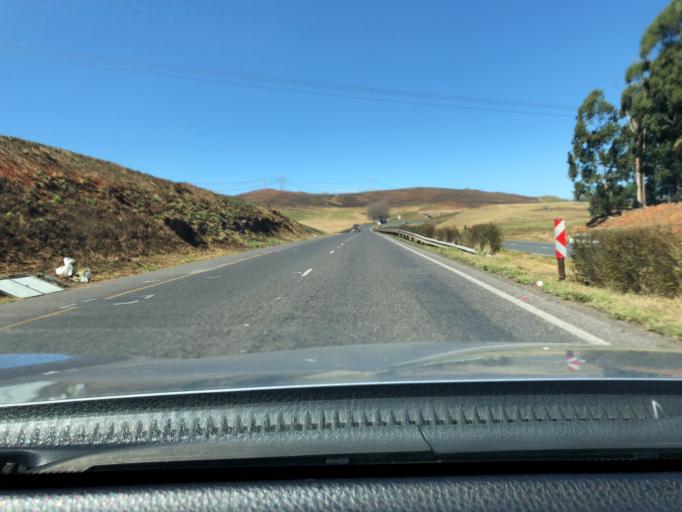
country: ZA
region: KwaZulu-Natal
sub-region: uMgungundlovu District Municipality
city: Howick
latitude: -29.4247
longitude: 30.1688
